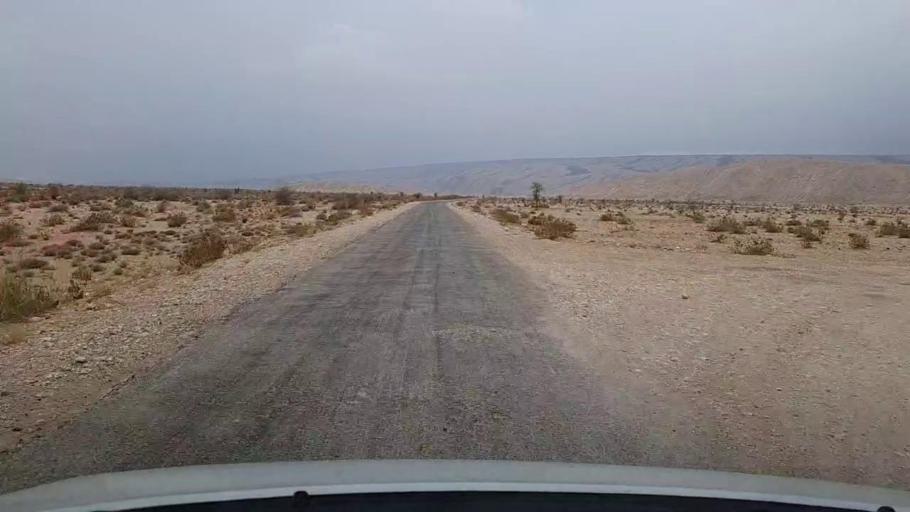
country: PK
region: Sindh
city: Sehwan
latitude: 26.2517
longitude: 67.7191
